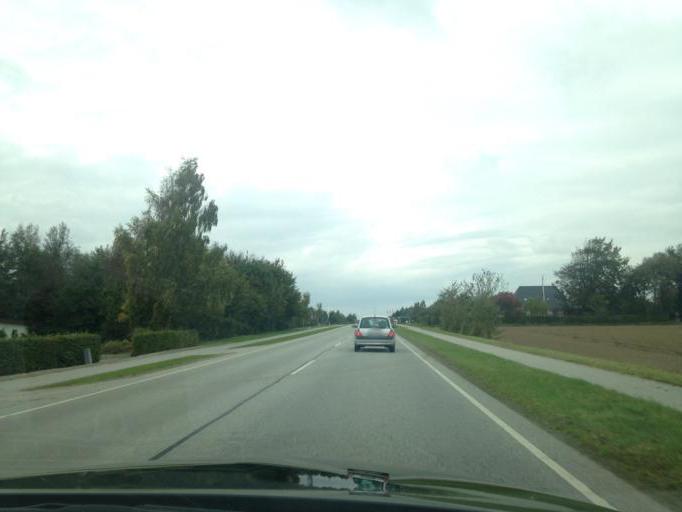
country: DK
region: South Denmark
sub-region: Kolding Kommune
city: Christiansfeld
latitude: 55.3215
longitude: 9.4949
